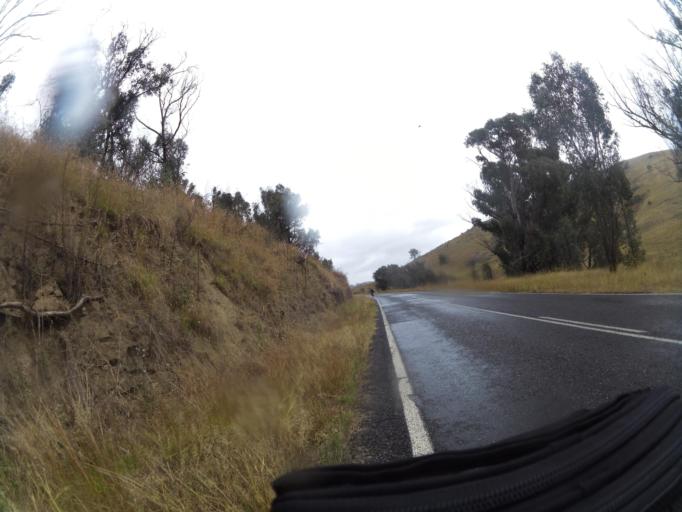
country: AU
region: New South Wales
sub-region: Greater Hume Shire
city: Holbrook
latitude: -36.2243
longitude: 147.7260
